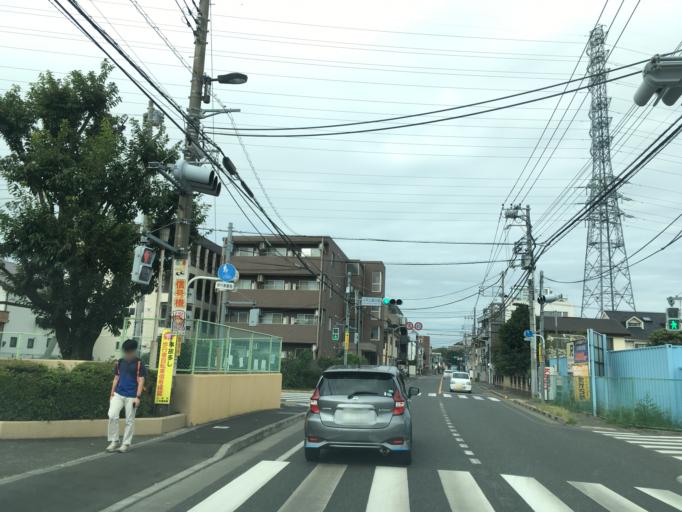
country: JP
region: Tokyo
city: Higashimurayama-shi
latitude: 35.7321
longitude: 139.4413
